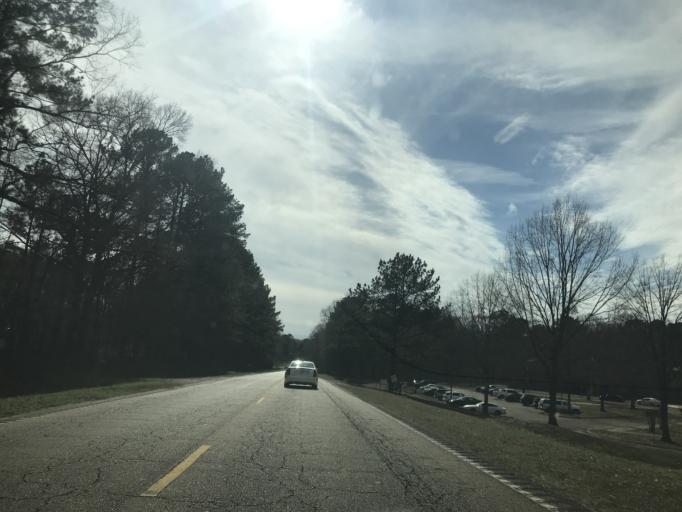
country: US
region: Mississippi
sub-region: Hinds County
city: Edwards
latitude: 32.1025
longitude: -90.6166
